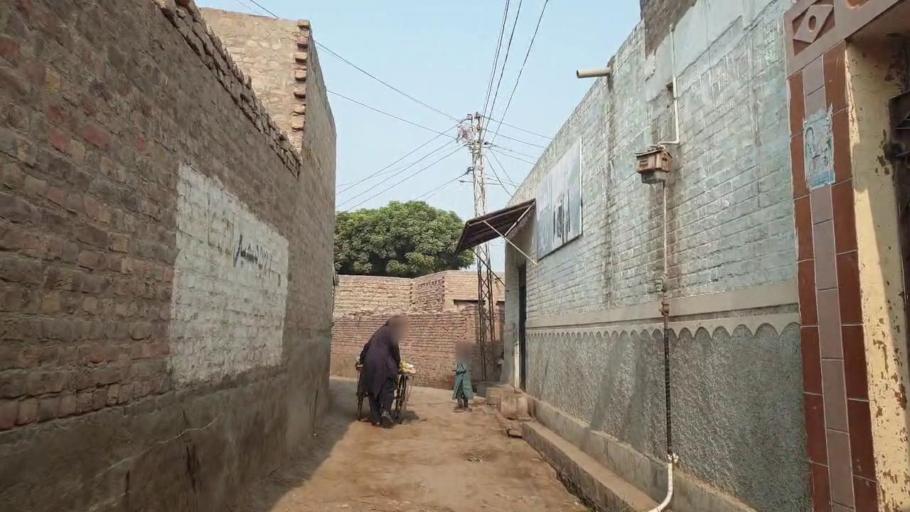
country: PK
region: Sindh
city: Tando Muhammad Khan
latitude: 25.1957
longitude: 68.5662
